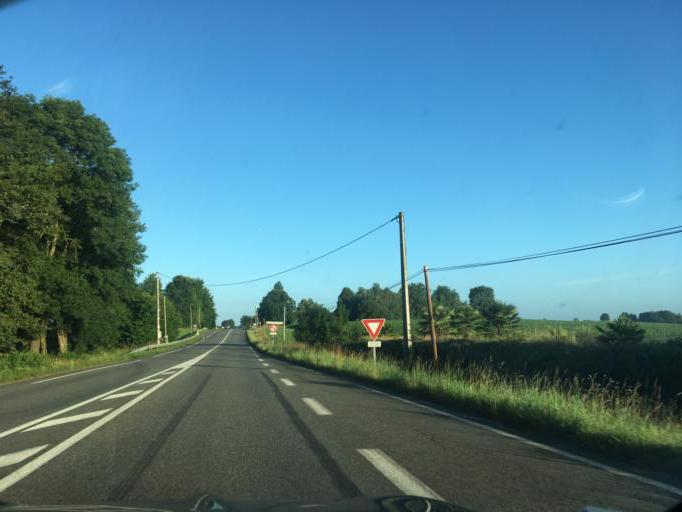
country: FR
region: Aquitaine
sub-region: Departement des Pyrenees-Atlantiques
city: Soumoulou
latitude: 43.2550
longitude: -0.1386
